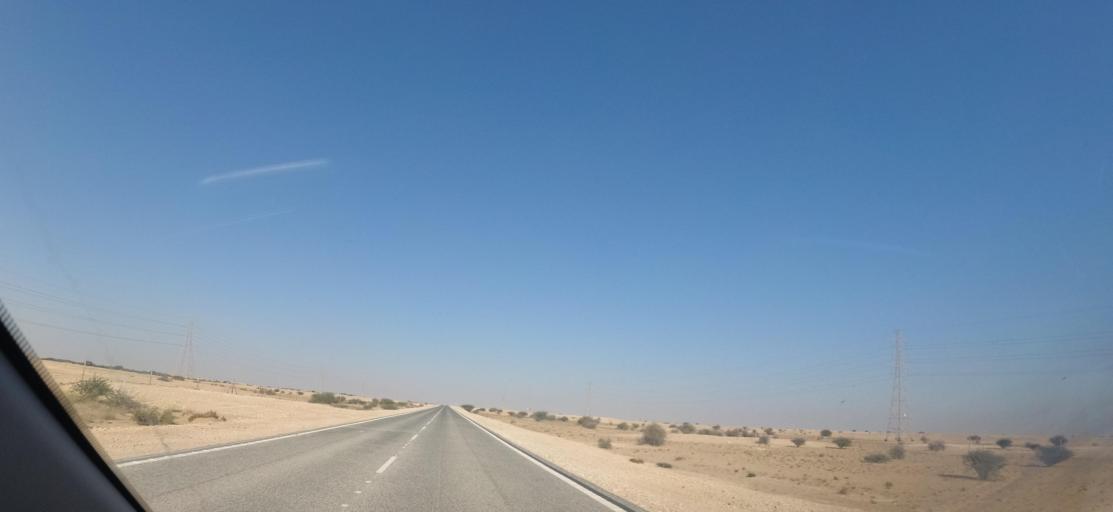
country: QA
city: Al Jumayliyah
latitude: 25.6462
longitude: 51.1081
